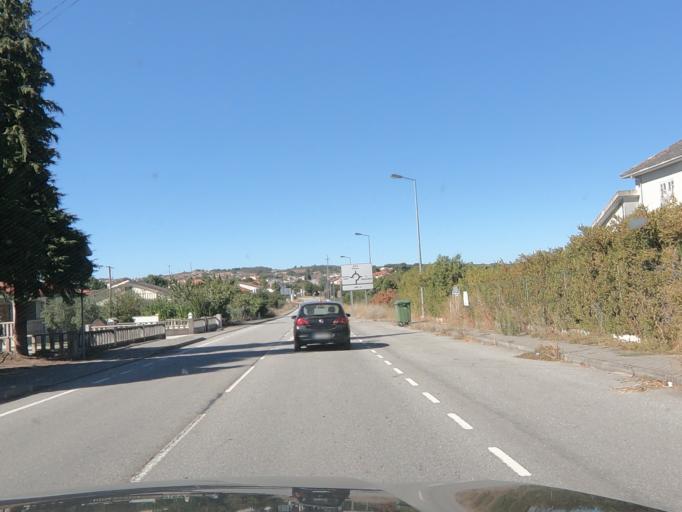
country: PT
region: Vila Real
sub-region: Valpacos
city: Valpacos
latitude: 41.6617
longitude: -7.3307
